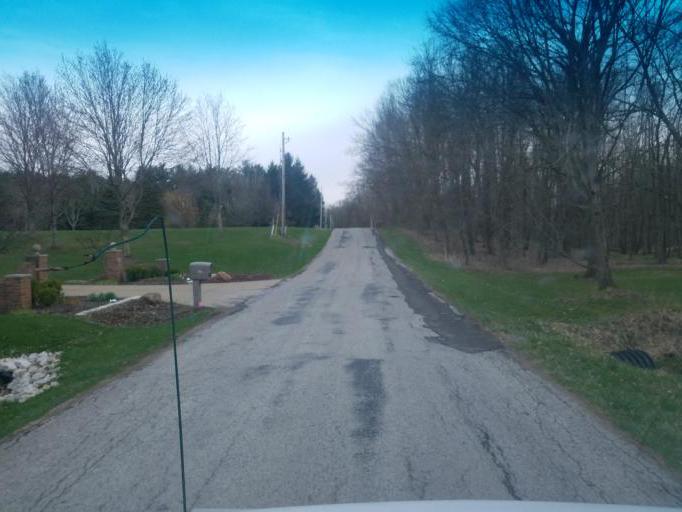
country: US
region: Ohio
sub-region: Richland County
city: Ontario
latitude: 40.7339
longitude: -82.6052
